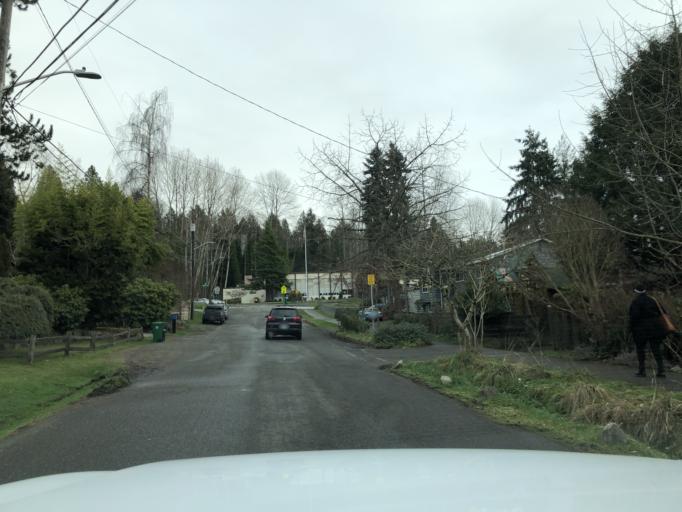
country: US
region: Washington
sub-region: King County
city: Lake Forest Park
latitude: 47.7076
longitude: -122.2866
